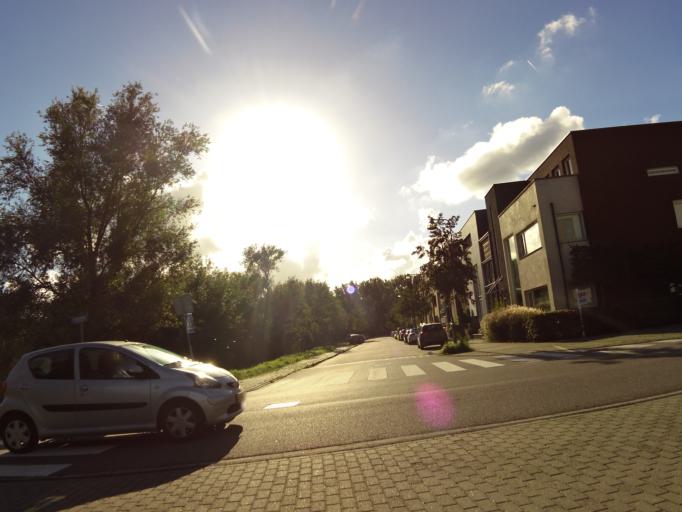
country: NL
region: South Holland
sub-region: Gemeente Leiderdorp
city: Leiderdorp
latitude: 52.1469
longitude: 4.5139
